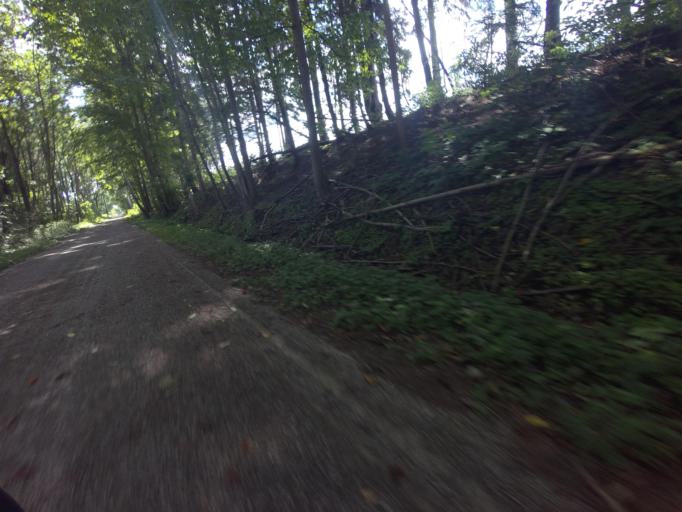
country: CA
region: Ontario
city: Huron East
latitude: 43.7189
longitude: -81.3936
